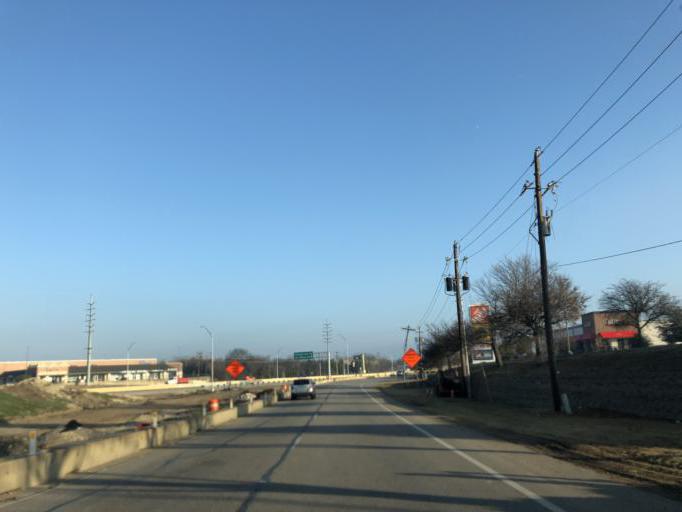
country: US
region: Texas
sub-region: Dallas County
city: Cedar Hill
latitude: 32.5957
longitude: -96.9386
